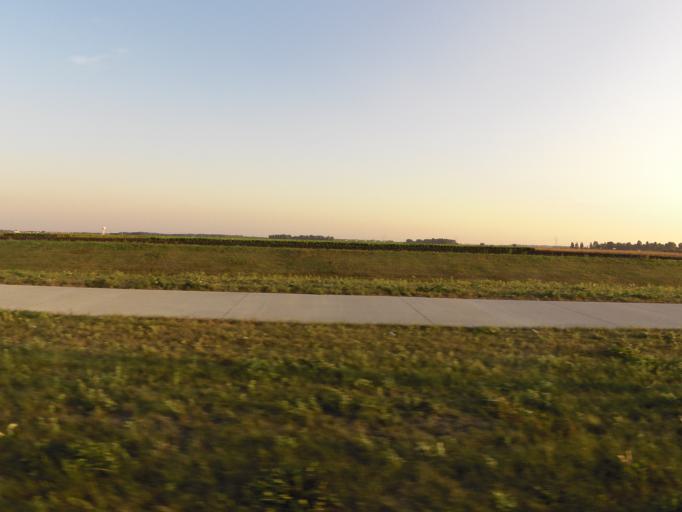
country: US
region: North Dakota
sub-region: Grand Forks County
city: Grand Forks
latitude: 47.8824
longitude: -97.0809
